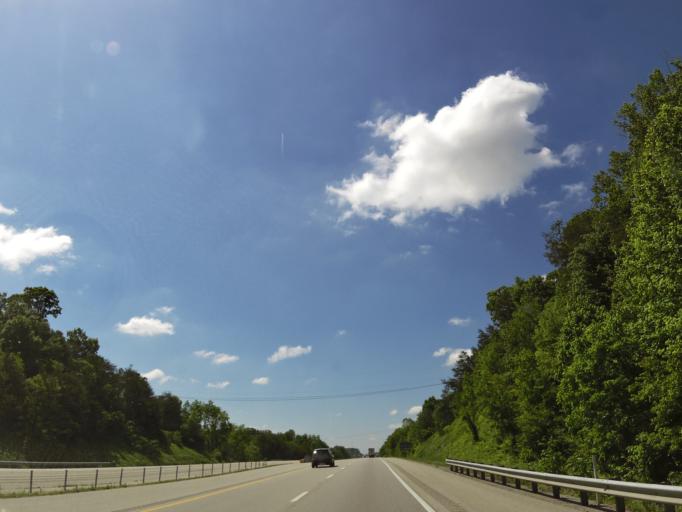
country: US
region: Kentucky
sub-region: Laurel County
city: London
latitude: 37.1585
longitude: -84.1135
